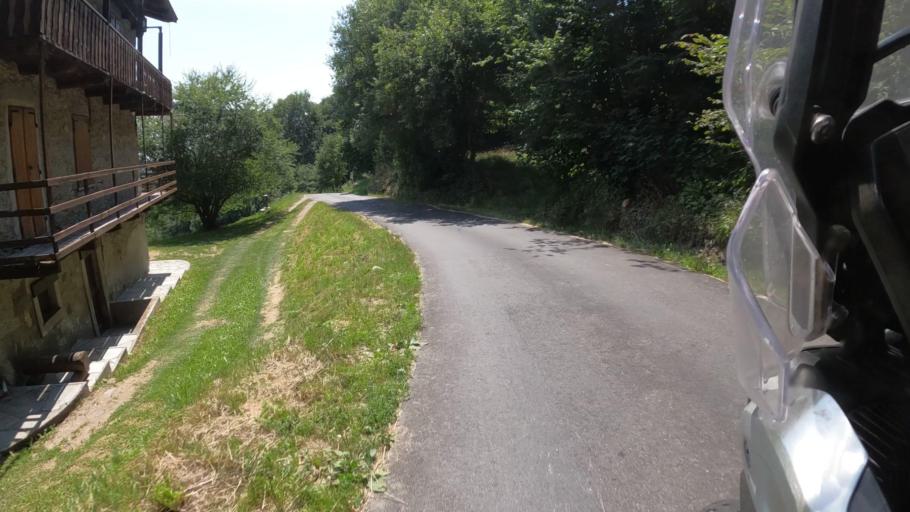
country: IT
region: Piedmont
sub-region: Provincia di Torino
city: Sant'Antonino di Susa
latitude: 45.1434
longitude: 7.2754
